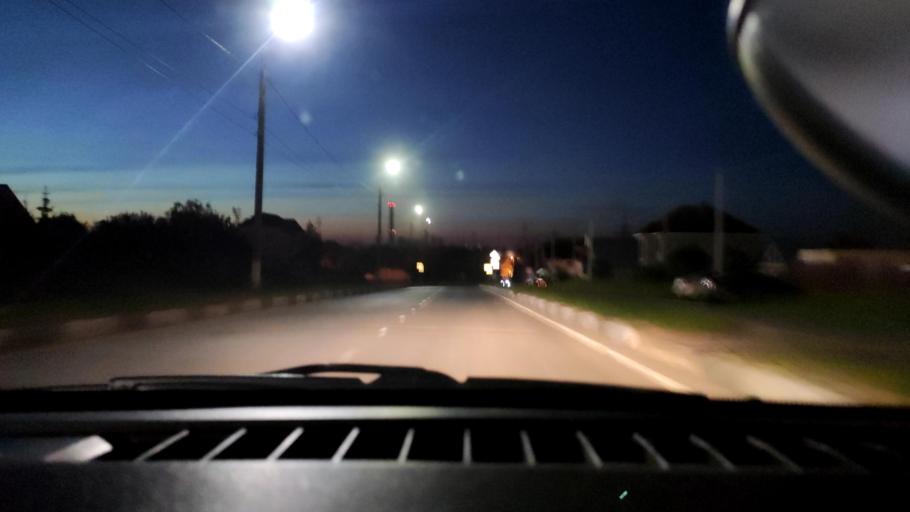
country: RU
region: Samara
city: Novokuybyshevsk
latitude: 53.0907
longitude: 49.9972
